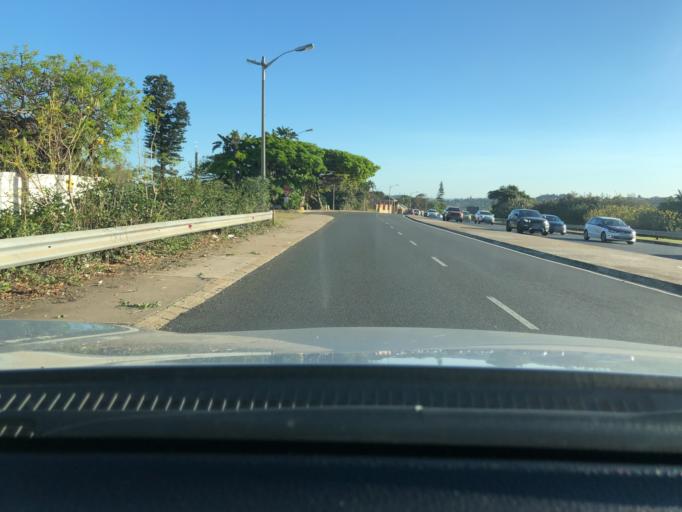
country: ZA
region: KwaZulu-Natal
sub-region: eThekwini Metropolitan Municipality
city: Umkomaas
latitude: -30.0382
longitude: 30.8985
